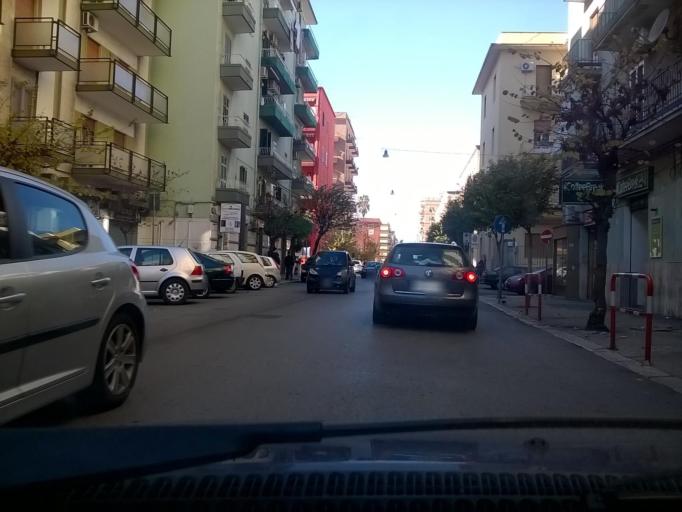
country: IT
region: Apulia
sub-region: Provincia di Taranto
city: Taranto
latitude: 40.4641
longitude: 17.2577
